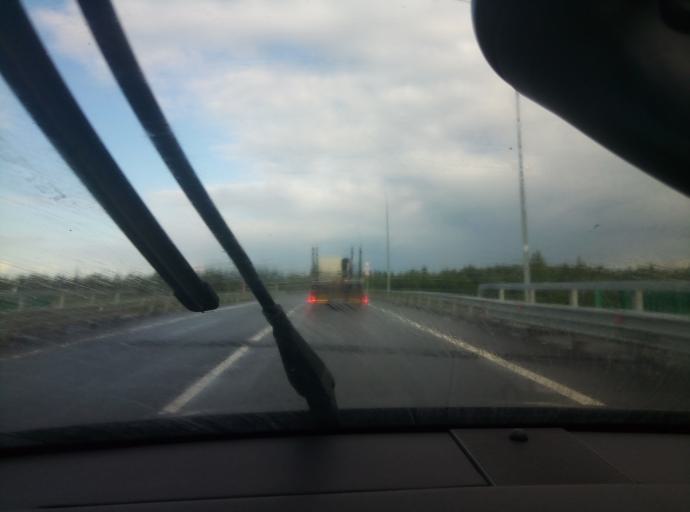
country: RU
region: Kaluga
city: Kurovskoye
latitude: 54.5272
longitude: 35.9850
